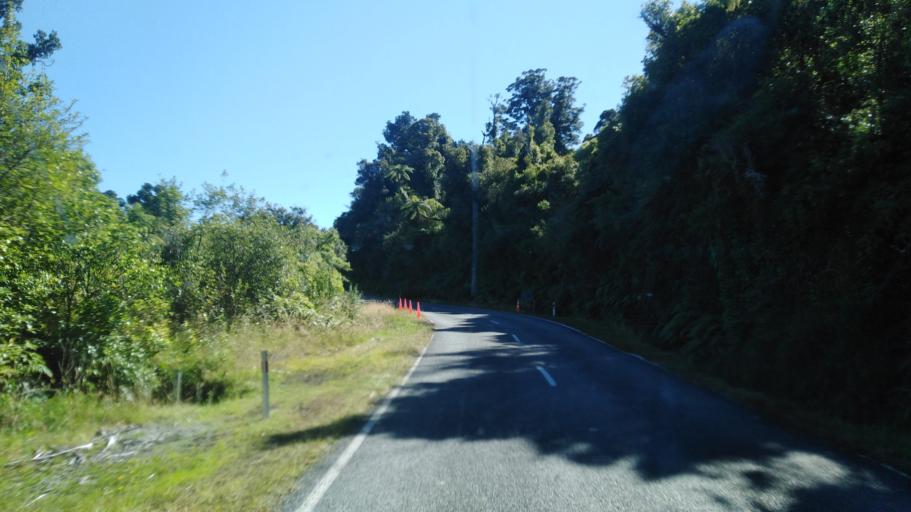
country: NZ
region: West Coast
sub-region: Buller District
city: Westport
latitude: -41.5285
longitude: 172.0084
